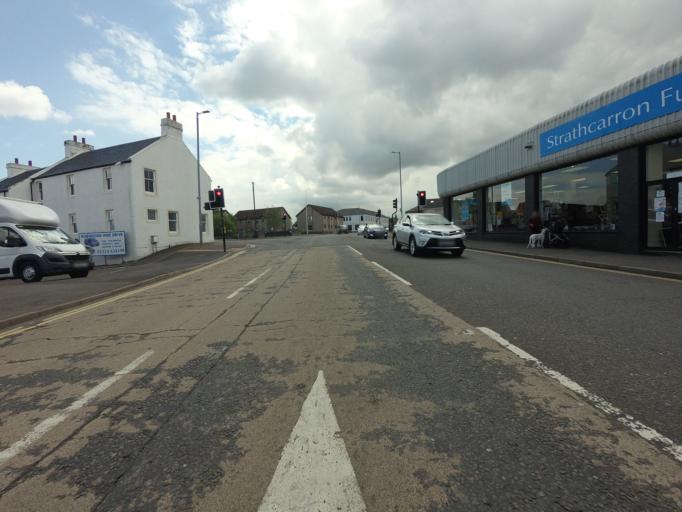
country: GB
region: Scotland
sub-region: Falkirk
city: Falkirk
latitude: 56.0110
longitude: -3.7859
